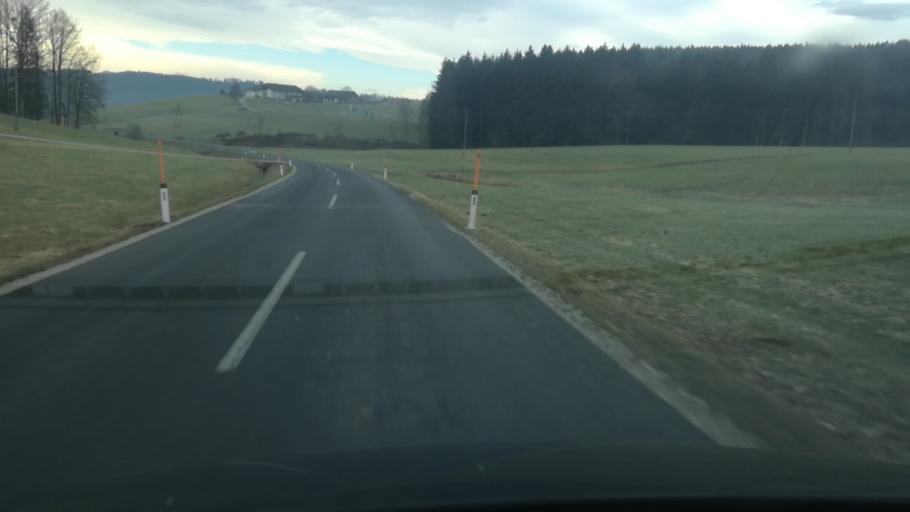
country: AT
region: Upper Austria
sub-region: Politischer Bezirk Vocklabruck
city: Neukirchen an der Vockla
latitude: 48.0378
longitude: 13.5362
